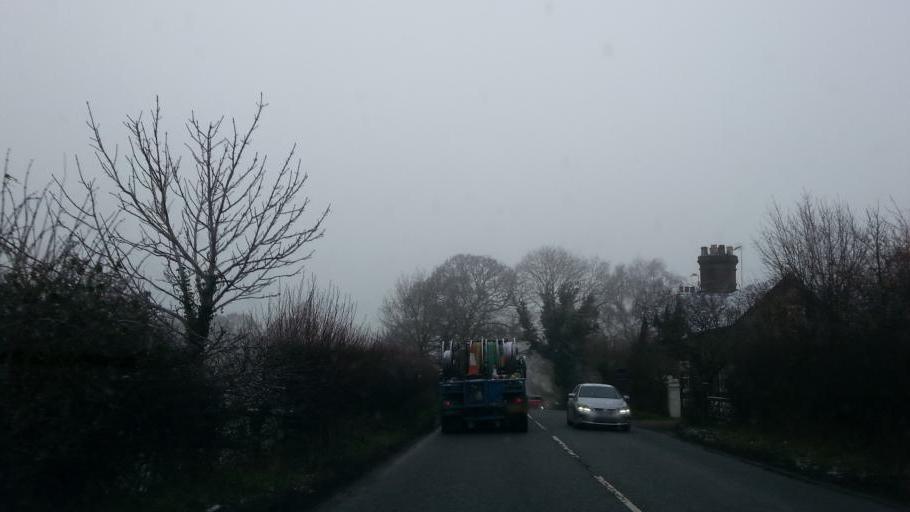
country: GB
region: England
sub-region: Cheshire East
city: Siddington
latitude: 53.2051
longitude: -2.2253
